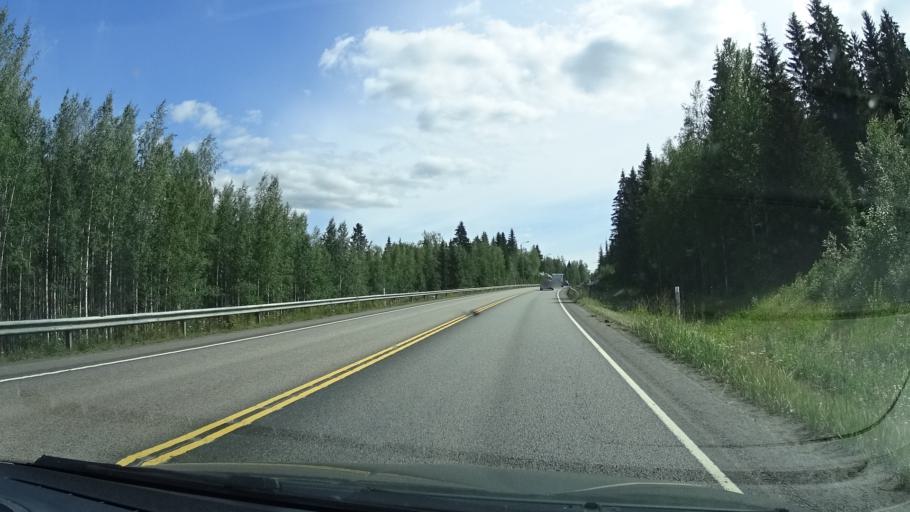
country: FI
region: Central Finland
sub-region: Jyvaeskylae
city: Jyvaeskylae
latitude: 62.2692
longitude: 25.5471
